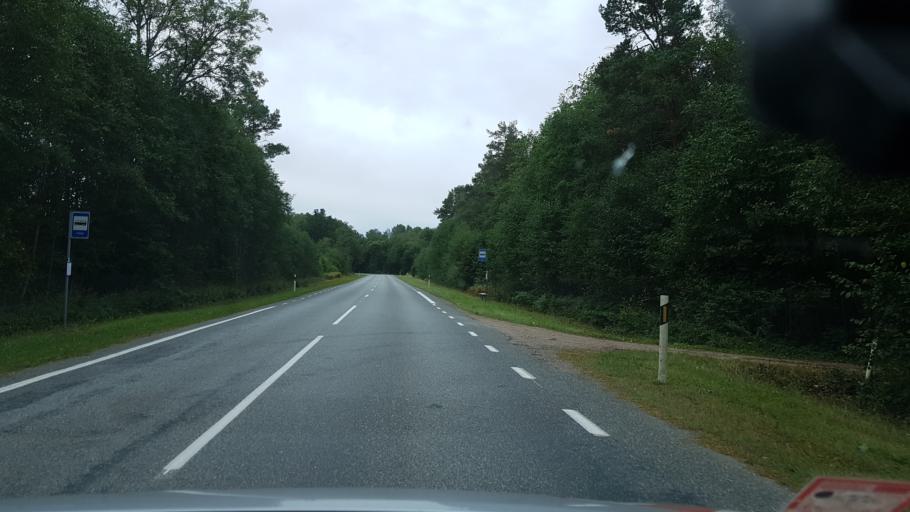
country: EE
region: Saare
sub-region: Kuressaare linn
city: Kuressaare
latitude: 58.4027
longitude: 22.6430
